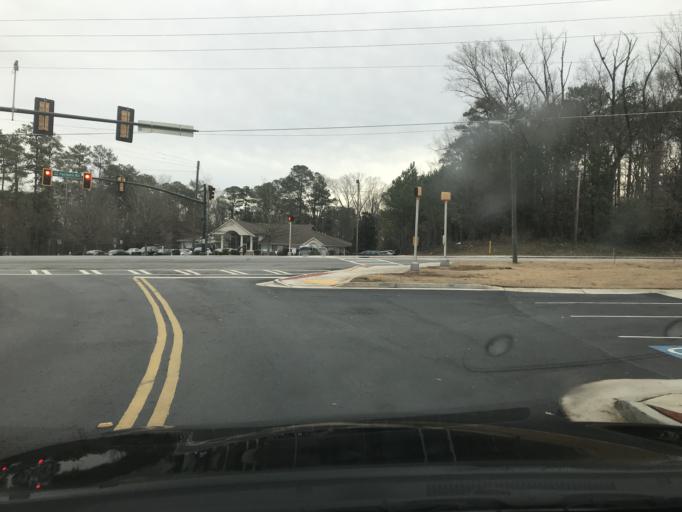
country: US
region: Georgia
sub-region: Fulton County
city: East Point
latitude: 33.7201
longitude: -84.5083
